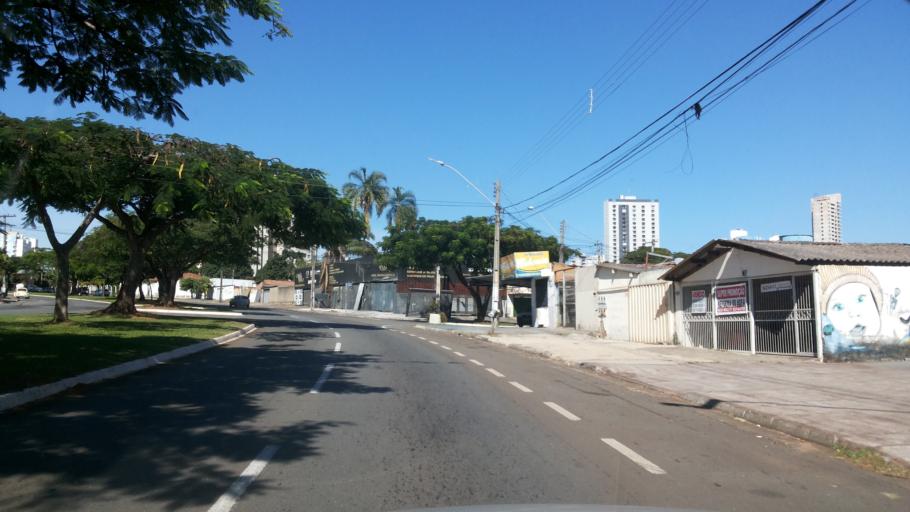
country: BR
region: Goias
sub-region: Goiania
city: Goiania
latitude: -16.7074
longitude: -49.2511
